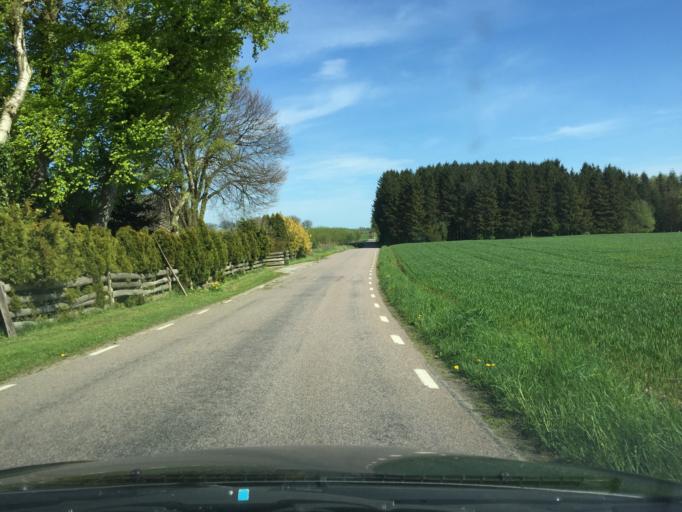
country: SE
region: Skane
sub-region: Sjobo Kommun
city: Blentarp
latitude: 55.5584
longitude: 13.5317
